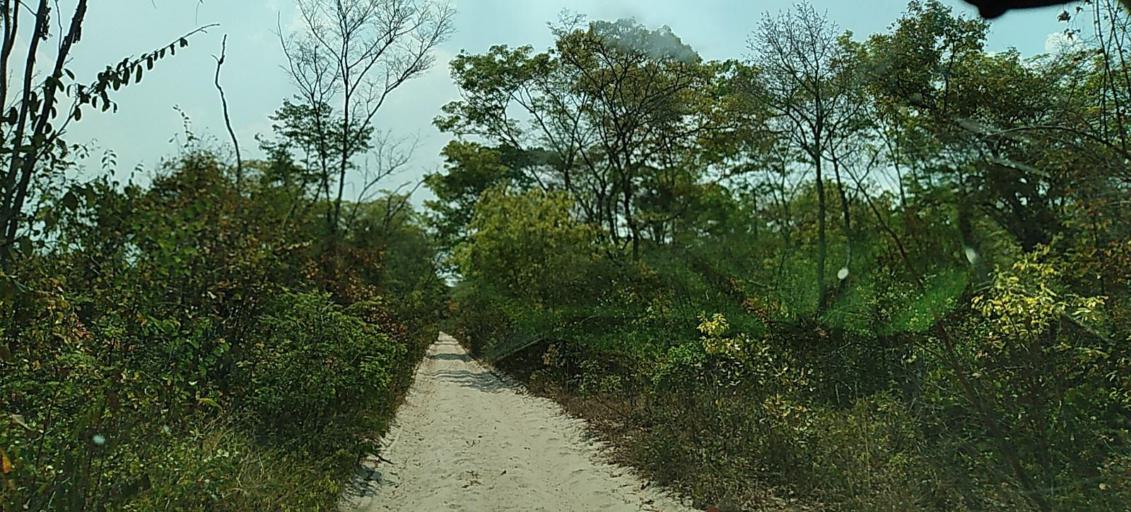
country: ZM
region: North-Western
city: Kabompo
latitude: -13.3957
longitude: 23.7981
